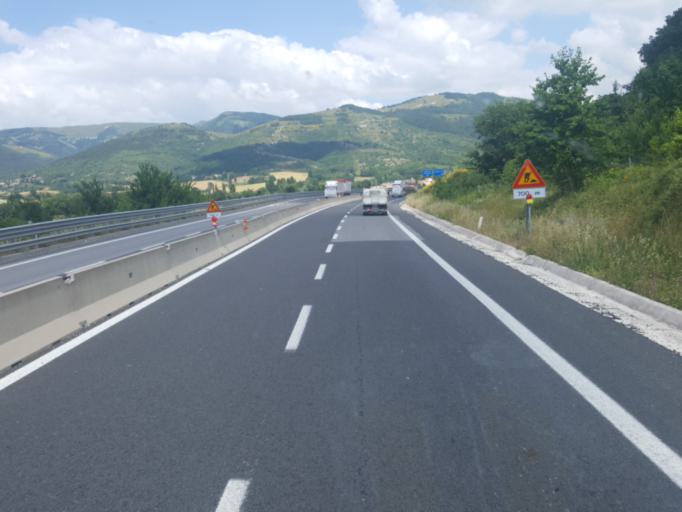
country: IT
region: Umbria
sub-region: Provincia di Perugia
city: Fossato di Vico
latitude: 43.2986
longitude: 12.7481
